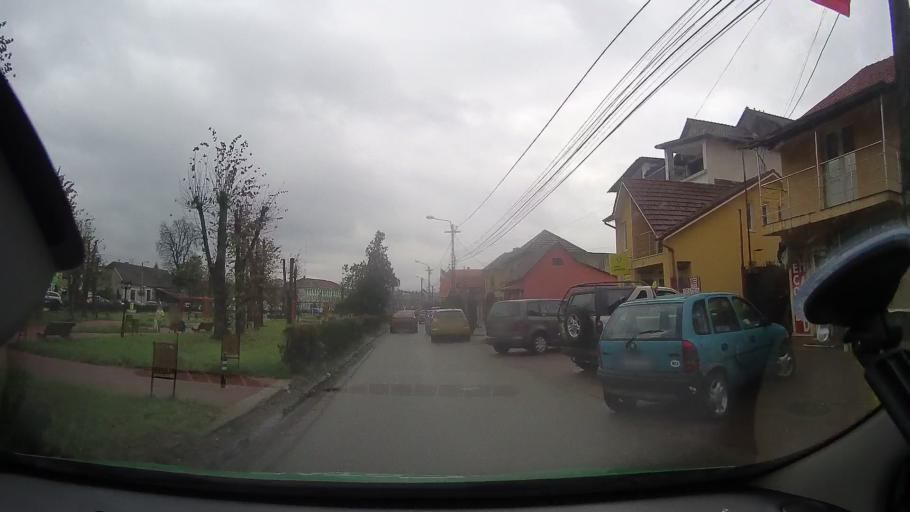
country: RO
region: Arad
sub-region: Comuna Sebis
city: Sebis
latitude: 46.3742
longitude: 22.1325
